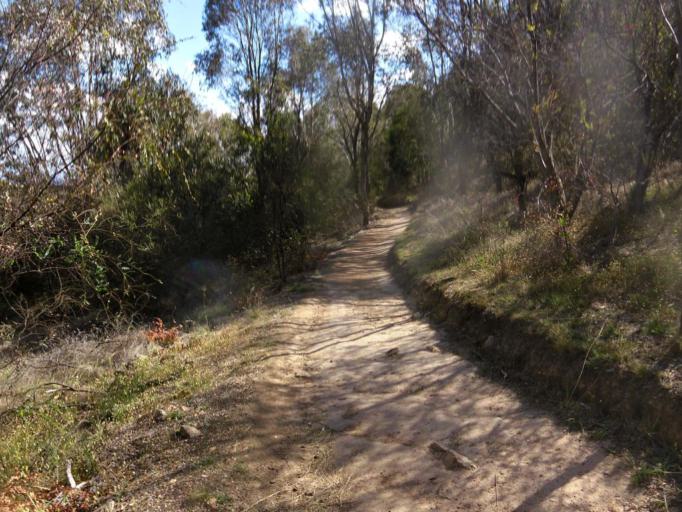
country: AU
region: Australian Capital Territory
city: Belconnen
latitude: -35.1597
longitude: 149.0763
